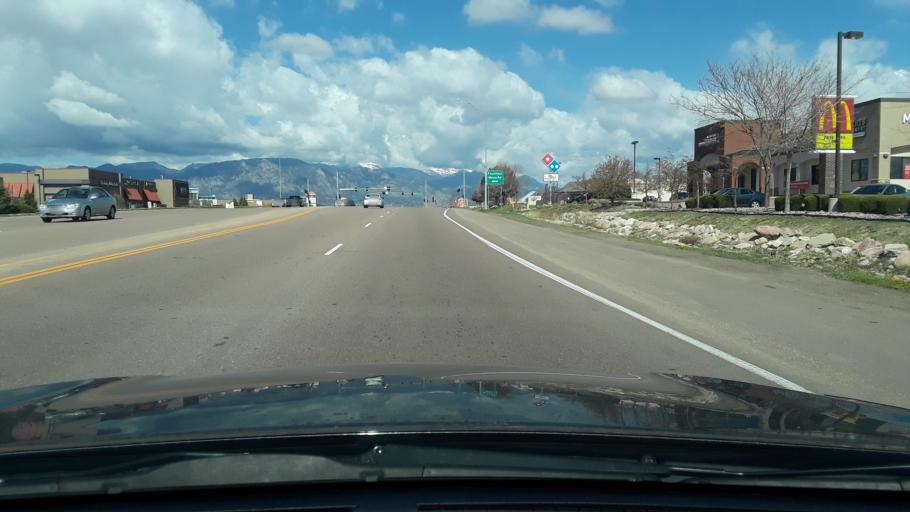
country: US
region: Colorado
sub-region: El Paso County
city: Security-Widefield
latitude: 38.7185
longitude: -104.6983
